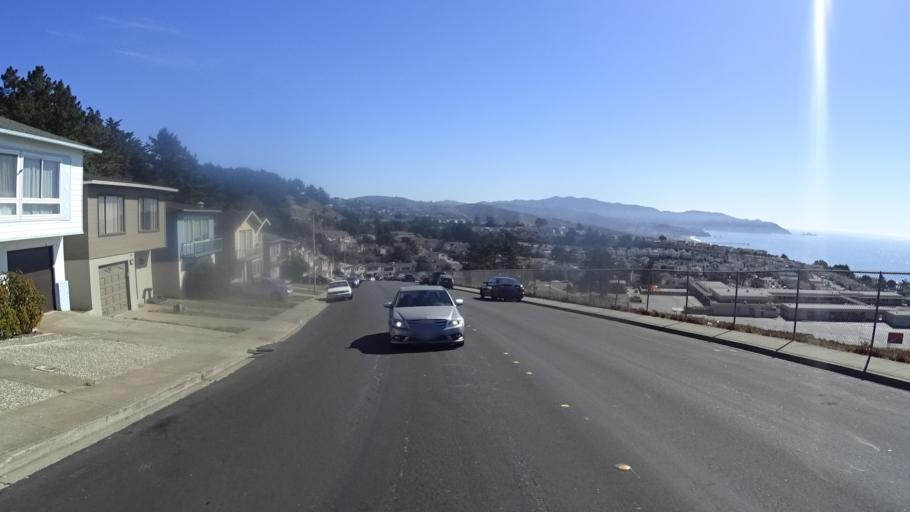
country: US
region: California
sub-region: San Mateo County
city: Broadmoor
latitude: 37.6641
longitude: -122.4865
